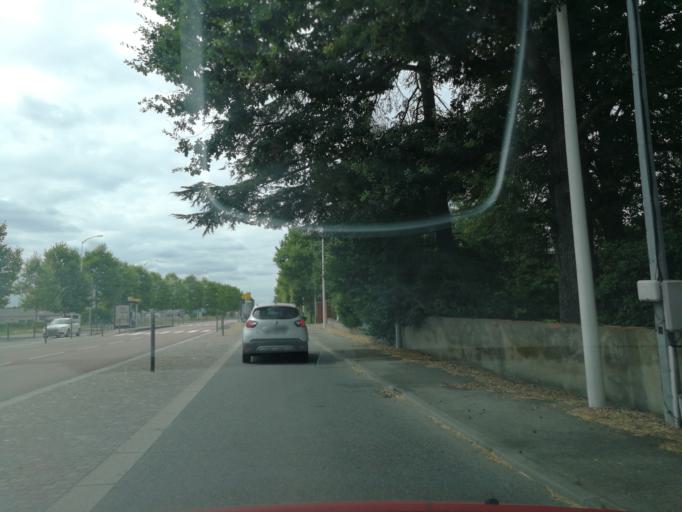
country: FR
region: Midi-Pyrenees
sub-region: Departement de la Haute-Garonne
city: Balma
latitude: 43.5886
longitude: 1.5167
